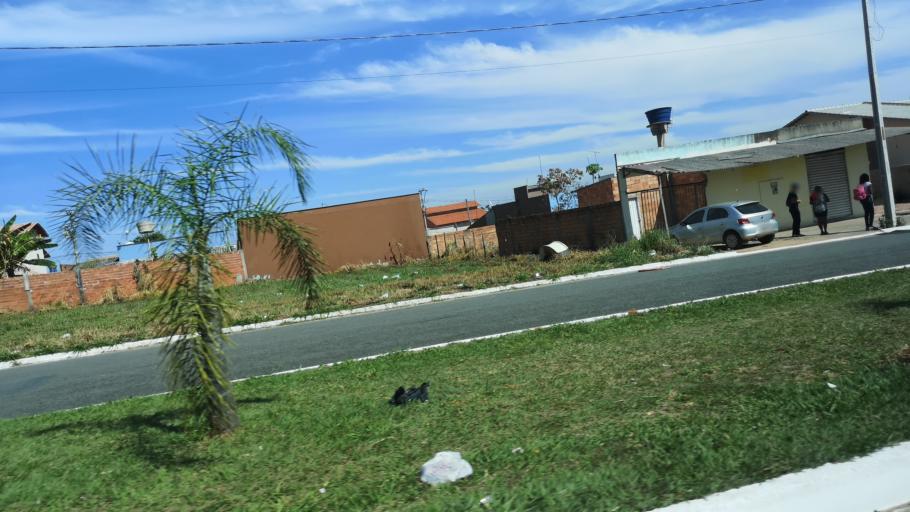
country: BR
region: Goias
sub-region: Senador Canedo
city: Senador Canedo
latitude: -16.6892
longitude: -49.0880
